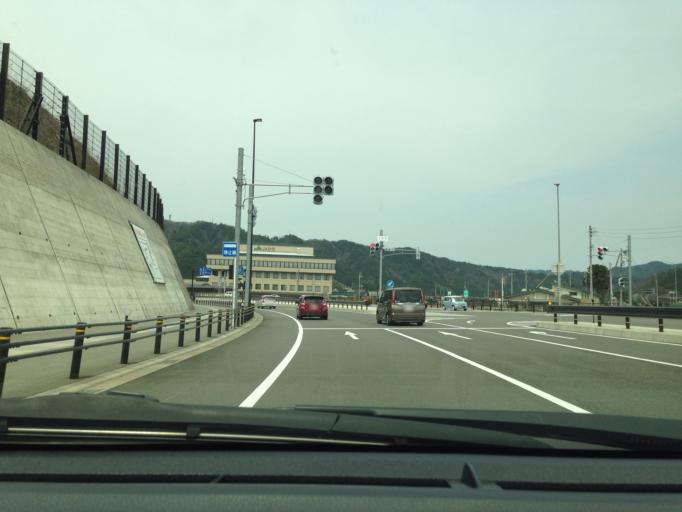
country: JP
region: Gifu
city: Takayama
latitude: 36.1600
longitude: 137.2439
